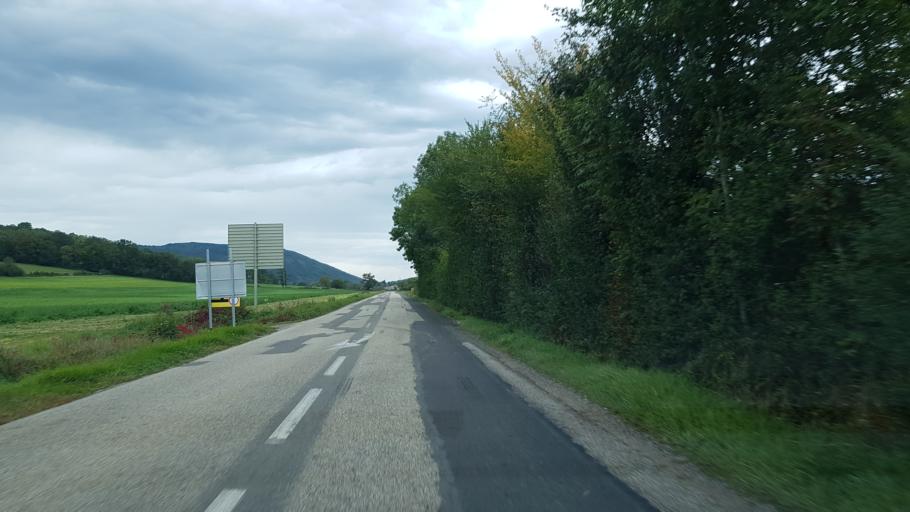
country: FR
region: Rhone-Alpes
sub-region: Departement de l'Ain
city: Cuisiat
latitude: 46.2480
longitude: 5.4234
